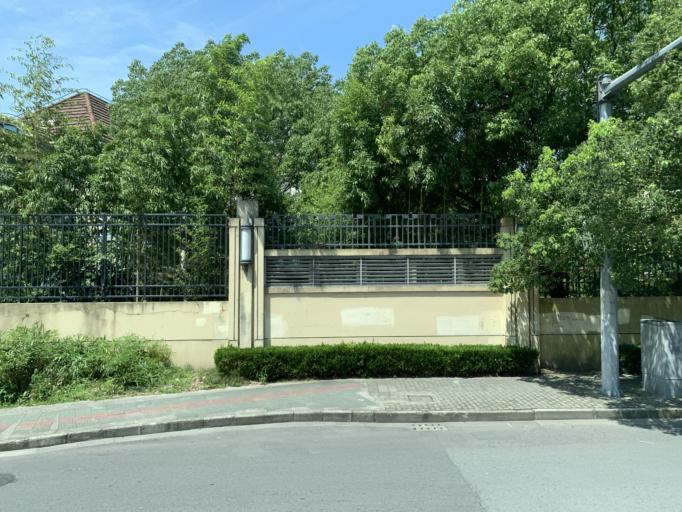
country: CN
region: Shanghai Shi
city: Huamu
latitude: 31.1781
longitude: 121.5342
